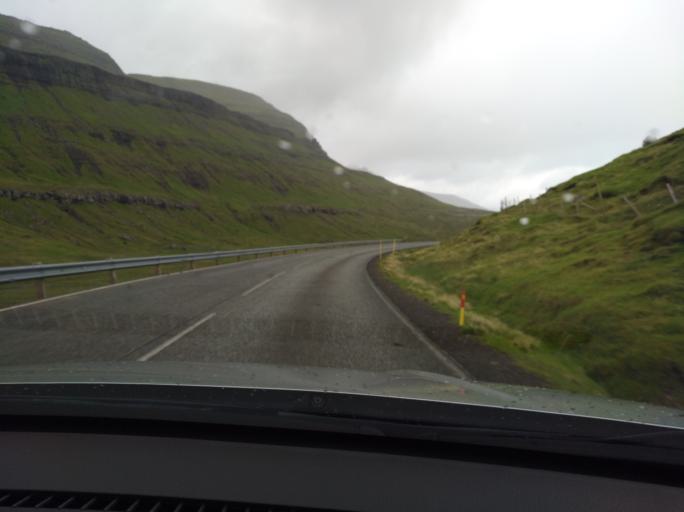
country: FO
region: Eysturoy
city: Fuglafjordur
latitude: 62.2320
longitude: -6.8805
